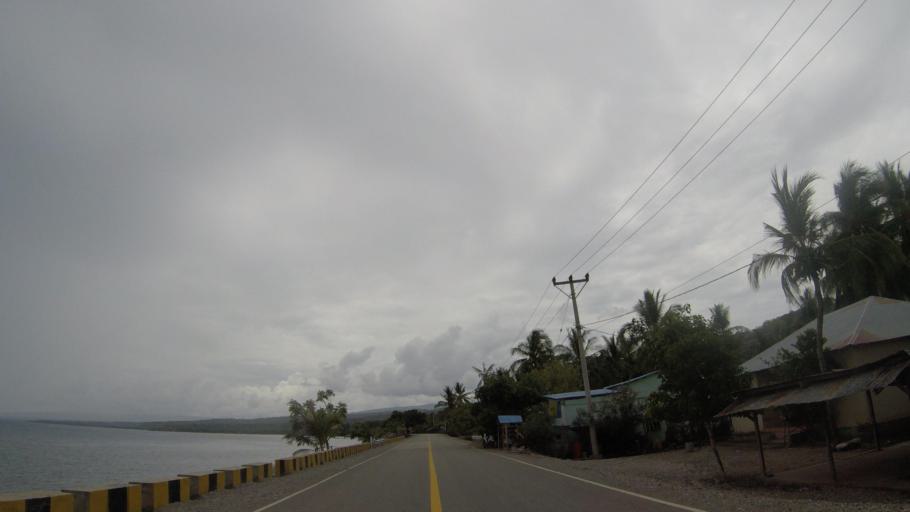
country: TL
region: Lautem
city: Lospalos
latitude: -8.4196
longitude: 126.7545
